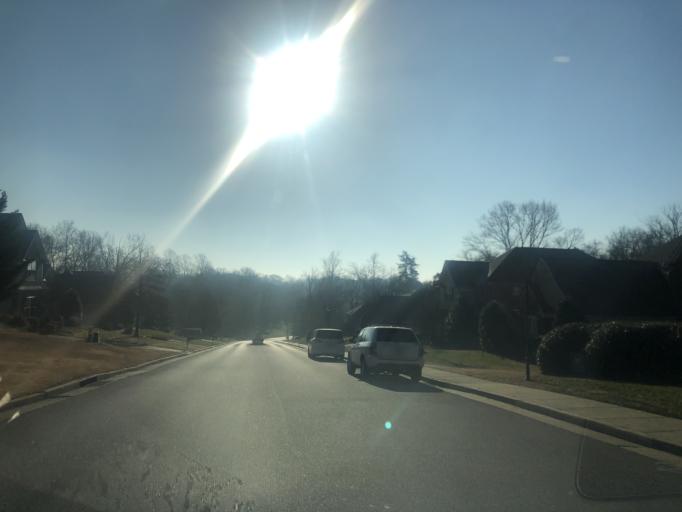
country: US
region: Tennessee
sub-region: Williamson County
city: Brentwood Estates
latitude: 35.9971
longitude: -86.7263
